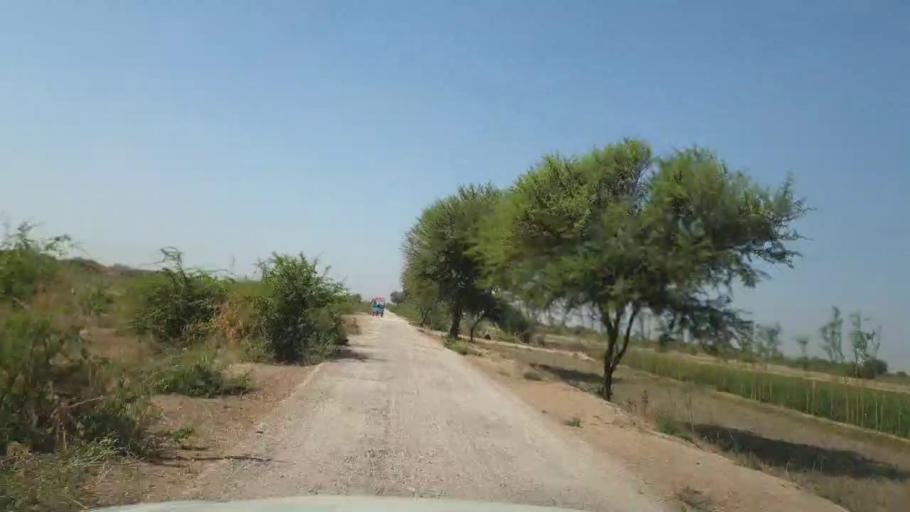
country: PK
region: Sindh
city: Kunri
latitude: 25.1137
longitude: 69.5300
